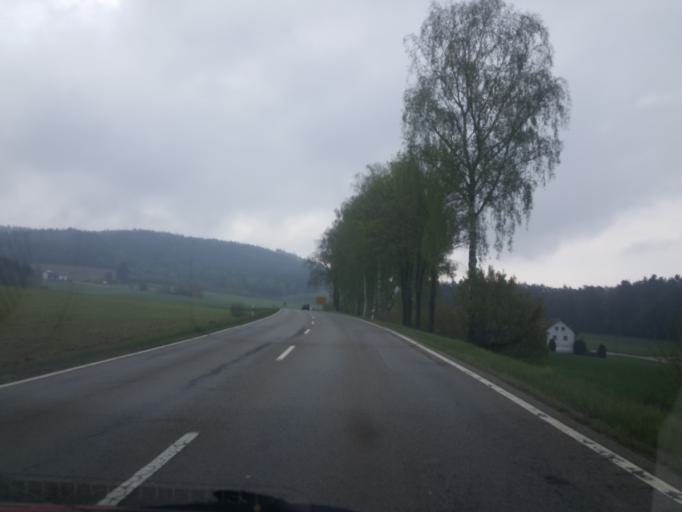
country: DE
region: Bavaria
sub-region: Lower Bavaria
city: Geiersthal
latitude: 49.0454
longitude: 12.9310
